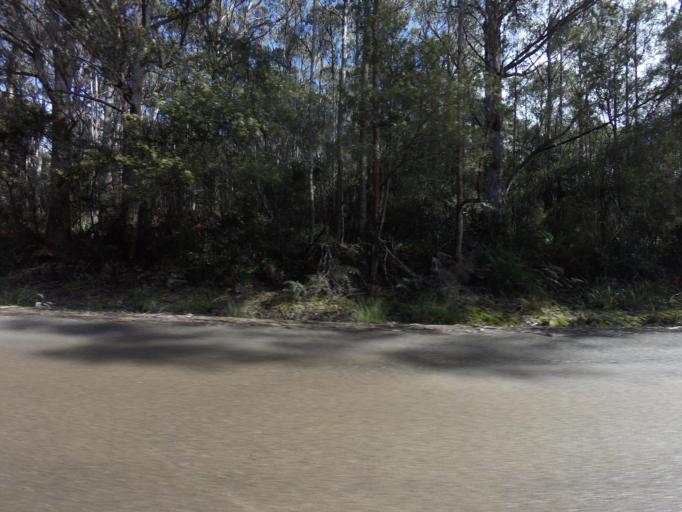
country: AU
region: Tasmania
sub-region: Huon Valley
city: Geeveston
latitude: -43.4139
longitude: 146.9113
